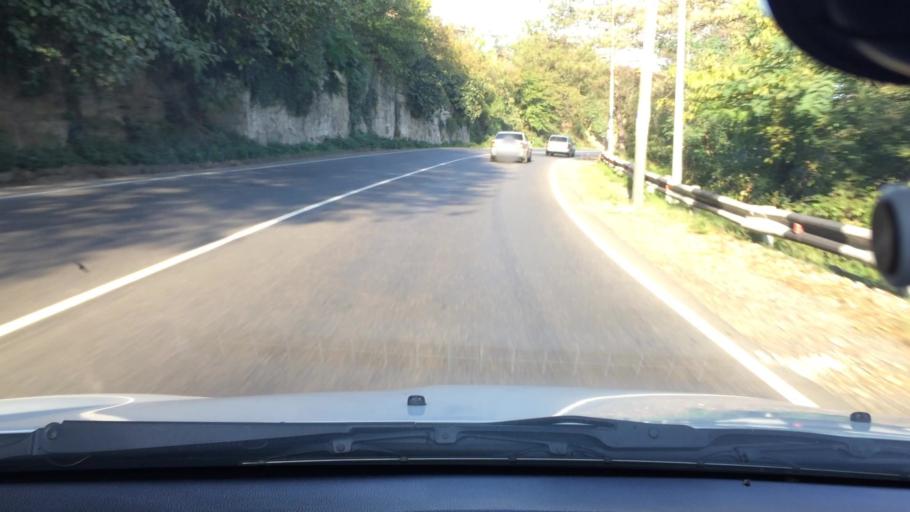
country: GE
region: Imereti
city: Zestap'oni
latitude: 42.1009
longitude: 43.0586
